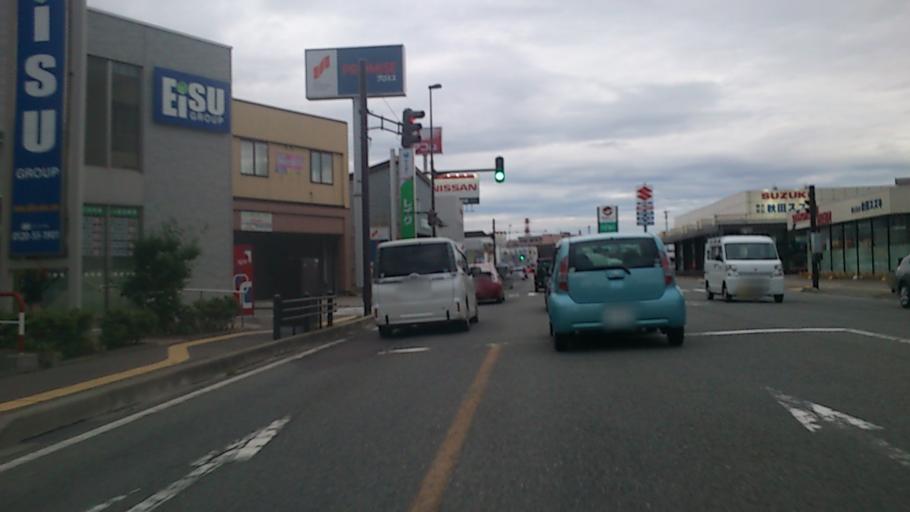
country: JP
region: Akita
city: Akita Shi
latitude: 39.7273
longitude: 140.1059
